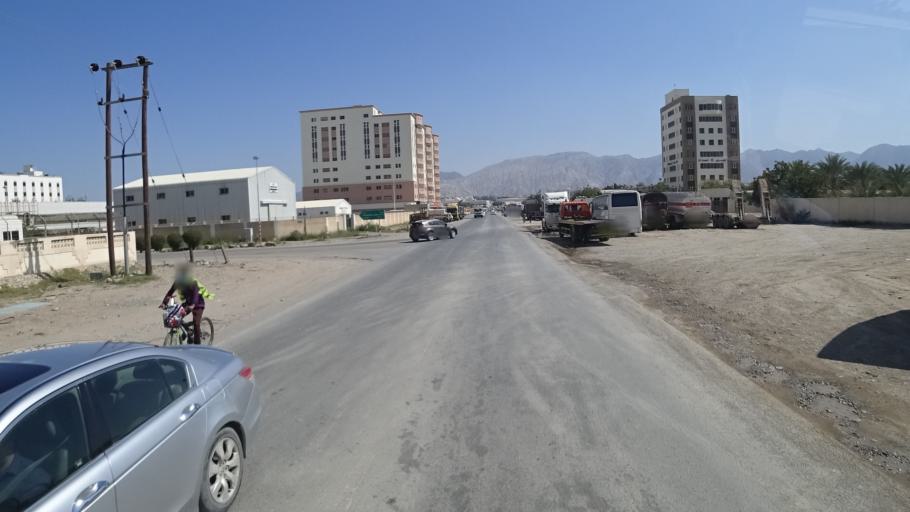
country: OM
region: Muhafazat Masqat
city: Bawshar
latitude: 23.5737
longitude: 58.3741
